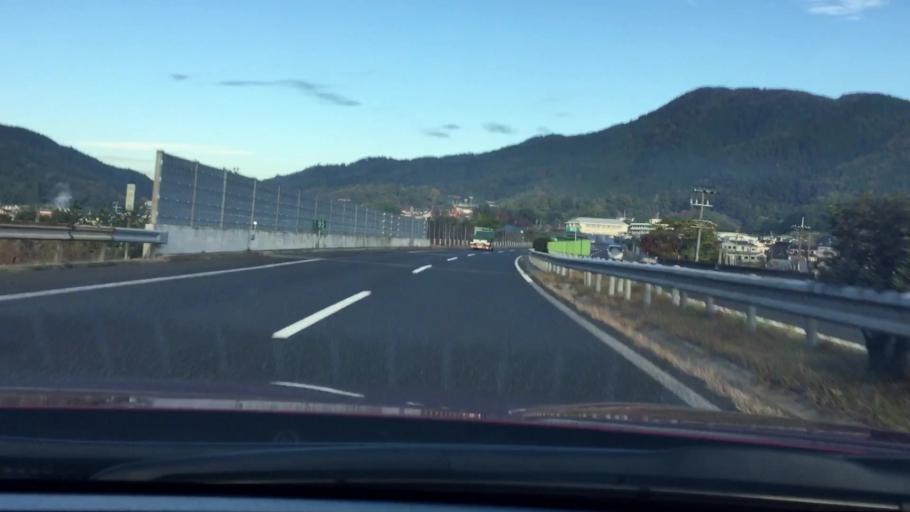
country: JP
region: Hyogo
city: Yamazakicho-nakabirose
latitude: 34.9859
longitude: 134.5994
